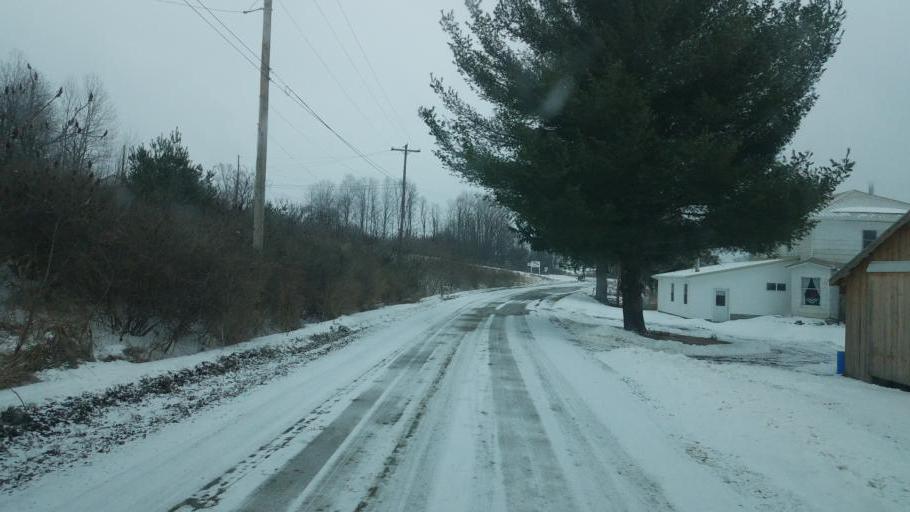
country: US
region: Pennsylvania
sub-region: Tioga County
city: Elkland
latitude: 42.1021
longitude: -77.4526
